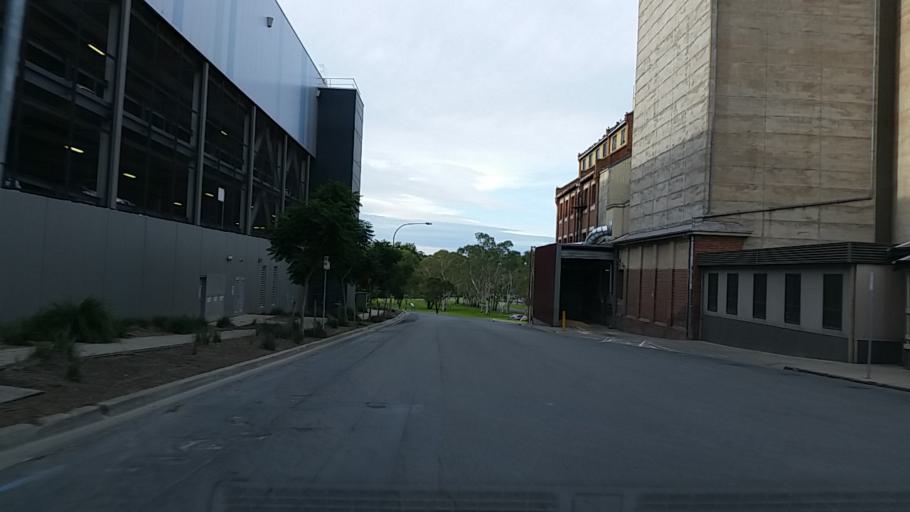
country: AU
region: South Australia
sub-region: Murray Bridge
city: Murray Bridge
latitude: -35.1196
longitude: 139.2787
